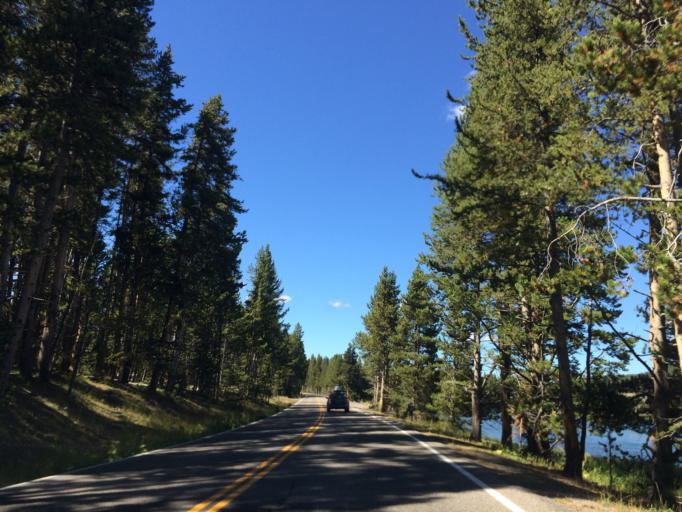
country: US
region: Montana
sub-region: Gallatin County
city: West Yellowstone
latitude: 44.6158
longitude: -110.4152
